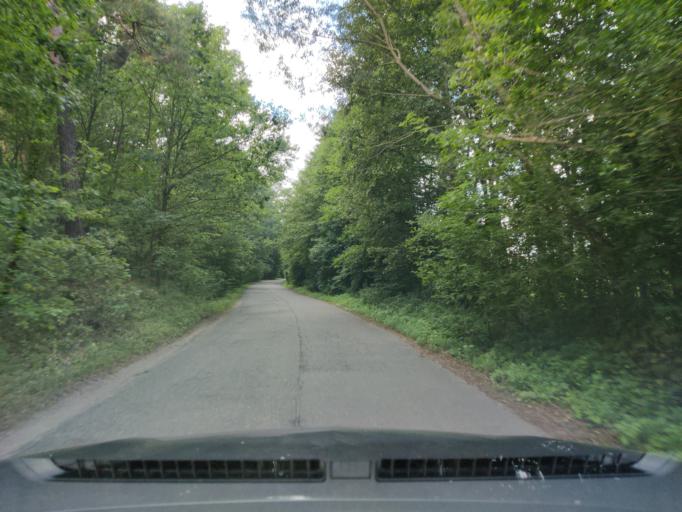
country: PL
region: Masovian Voivodeship
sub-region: Powiat pultuski
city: Pultusk
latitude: 52.7164
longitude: 21.1250
